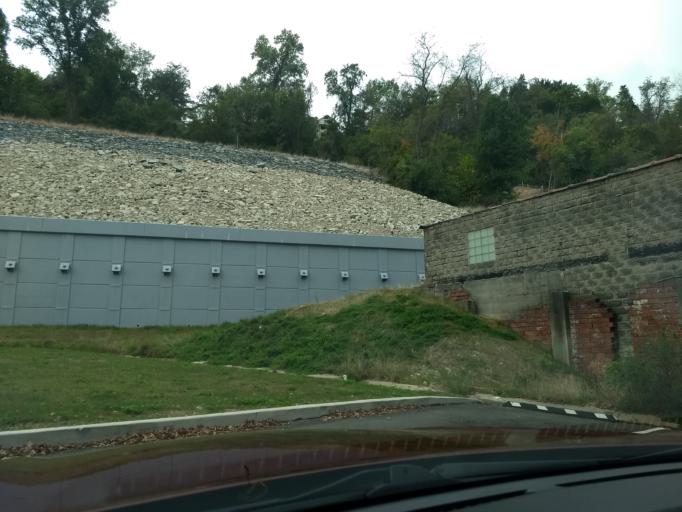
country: US
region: Pennsylvania
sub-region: Allegheny County
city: North Braddock
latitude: 40.4022
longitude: -79.8372
